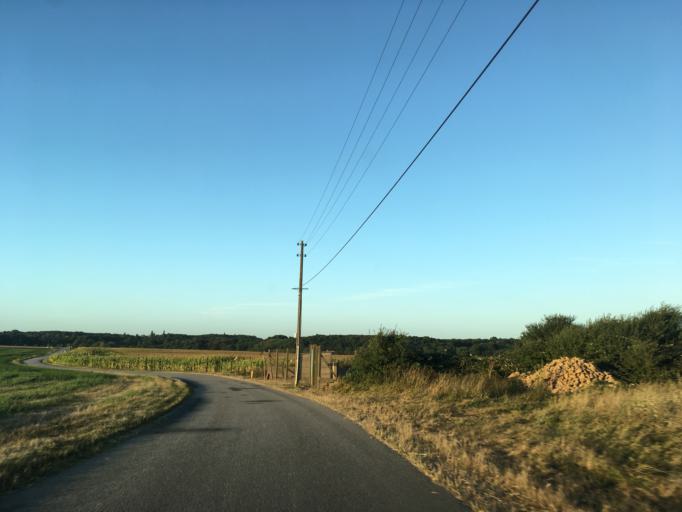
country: FR
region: Haute-Normandie
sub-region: Departement de l'Eure
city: Houlbec-Cocherel
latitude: 49.0578
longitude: 1.3619
